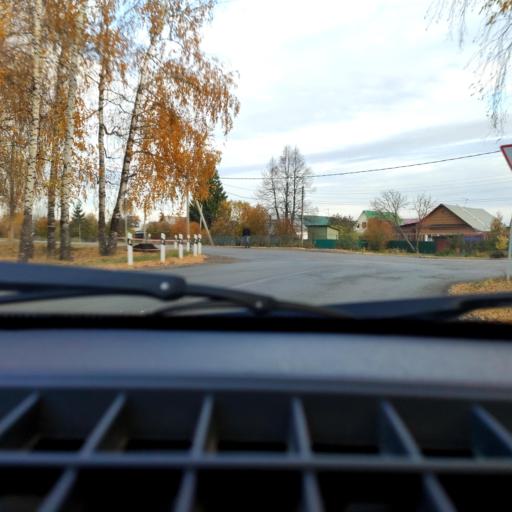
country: RU
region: Bashkortostan
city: Avdon
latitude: 54.6929
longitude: 55.7989
